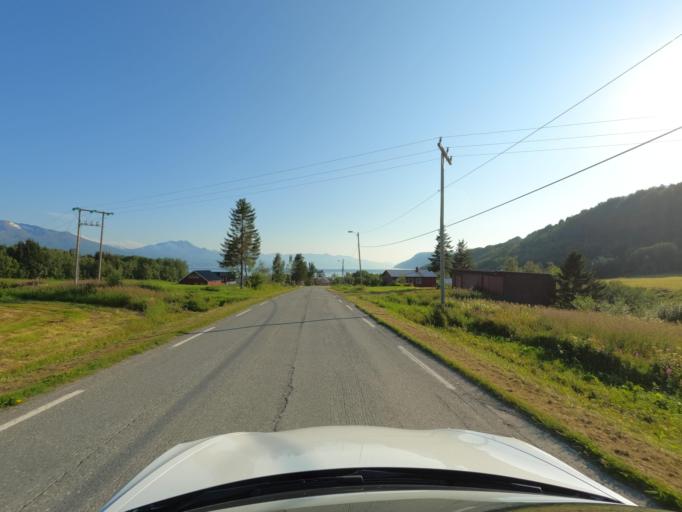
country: NO
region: Nordland
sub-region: Narvik
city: Bjerkvik
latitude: 68.5334
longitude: 17.4777
